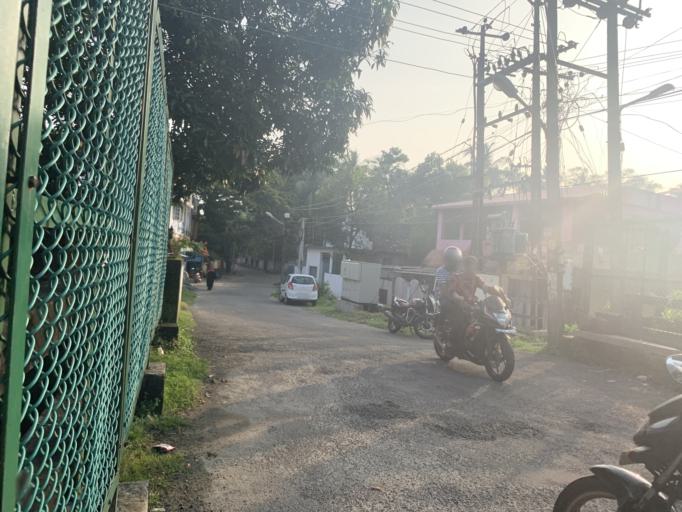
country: IN
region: Kerala
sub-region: Ernakulam
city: Cochin
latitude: 9.9609
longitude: 76.2498
